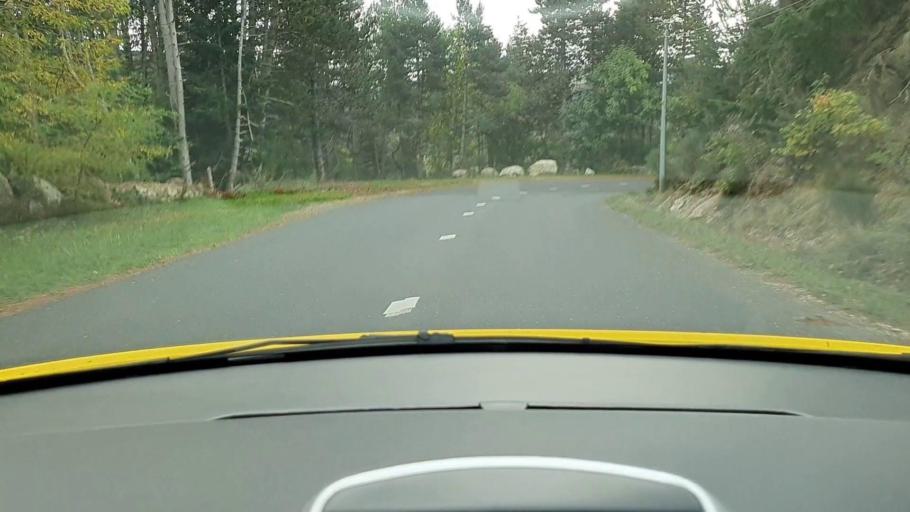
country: FR
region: Languedoc-Roussillon
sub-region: Departement de la Lozere
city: Meyrueis
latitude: 44.0758
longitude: 3.4665
